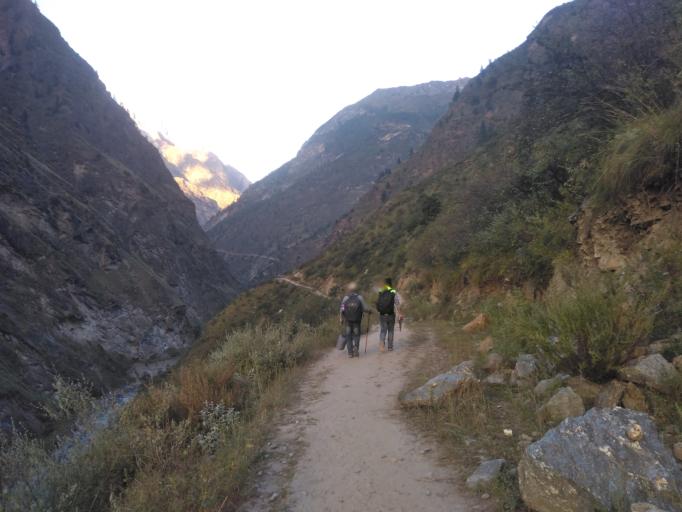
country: NP
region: Western Region
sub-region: Dhawalagiri Zone
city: Jomsom
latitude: 28.8772
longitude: 83.0068
